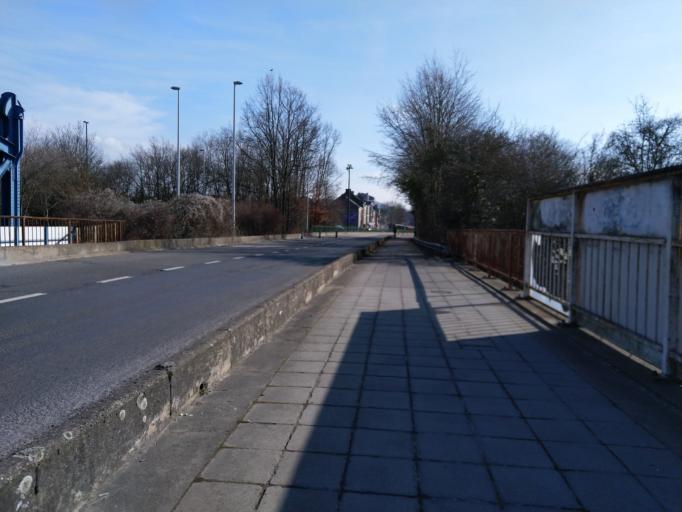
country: BE
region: Wallonia
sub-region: Province du Hainaut
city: Mons
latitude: 50.4501
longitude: 3.9375
